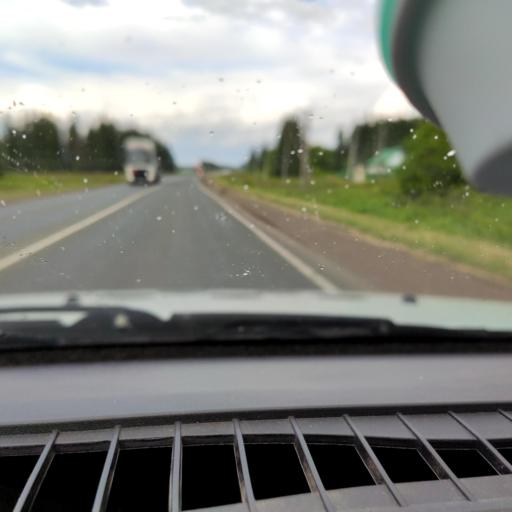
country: RU
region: Perm
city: Orda
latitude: 57.2025
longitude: 56.9213
